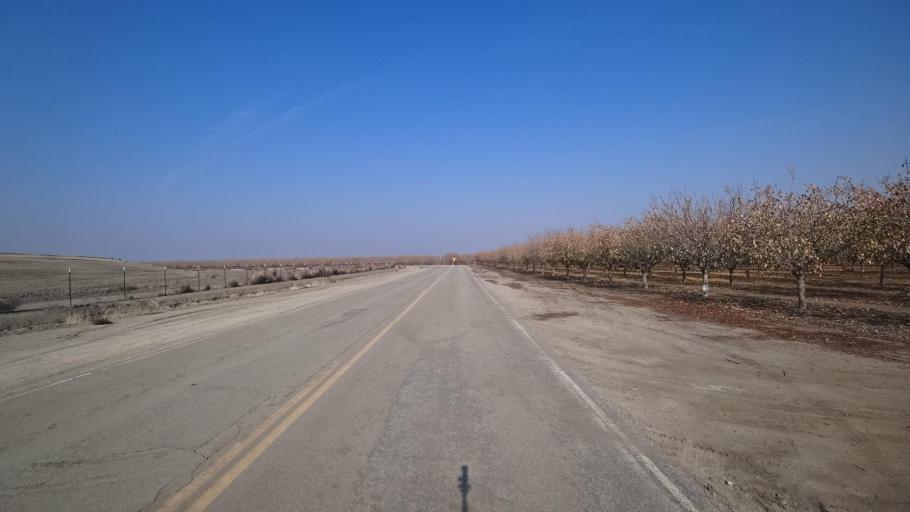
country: US
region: California
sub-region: Kern County
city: Buttonwillow
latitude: 35.3390
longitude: -119.3767
